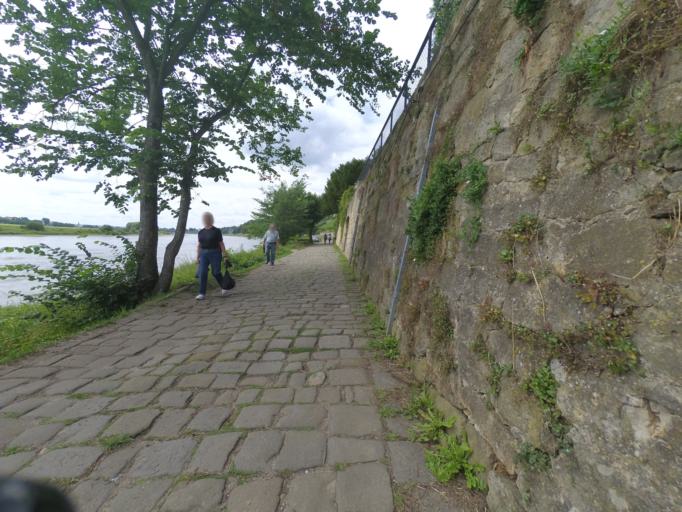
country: DE
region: Saxony
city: Albertstadt
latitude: 51.0608
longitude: 13.8042
